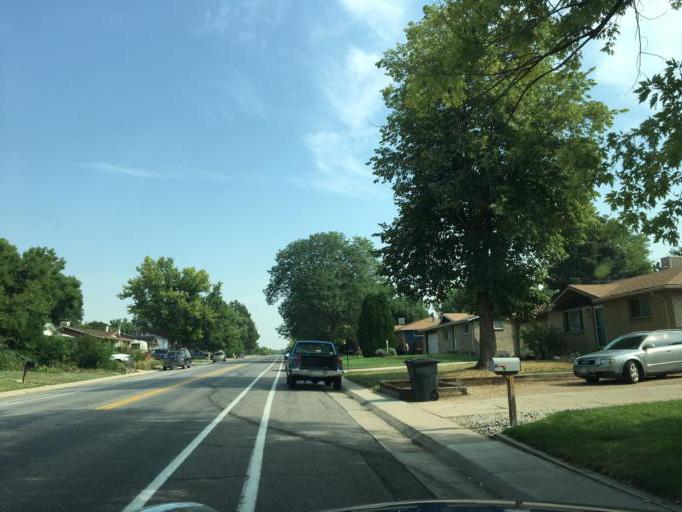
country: US
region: Colorado
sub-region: Jefferson County
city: Arvada
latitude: 39.8141
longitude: -105.0673
